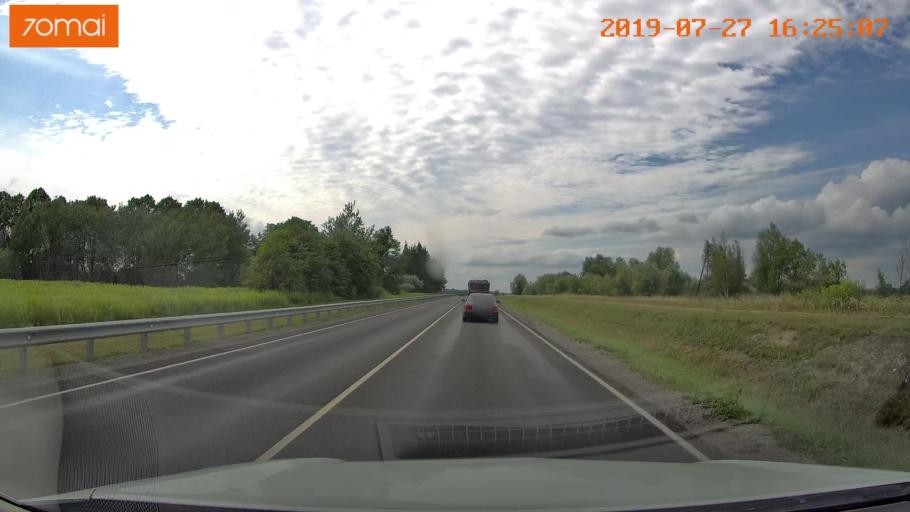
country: RU
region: Kaliningrad
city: Zheleznodorozhnyy
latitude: 54.6363
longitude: 21.4379
